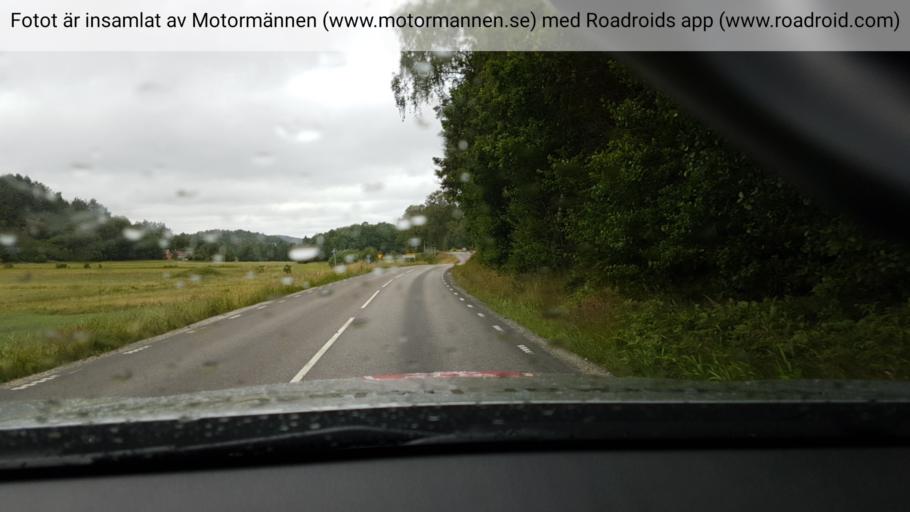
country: SE
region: Vaestra Goetaland
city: Svanesund
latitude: 58.1169
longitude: 11.8545
